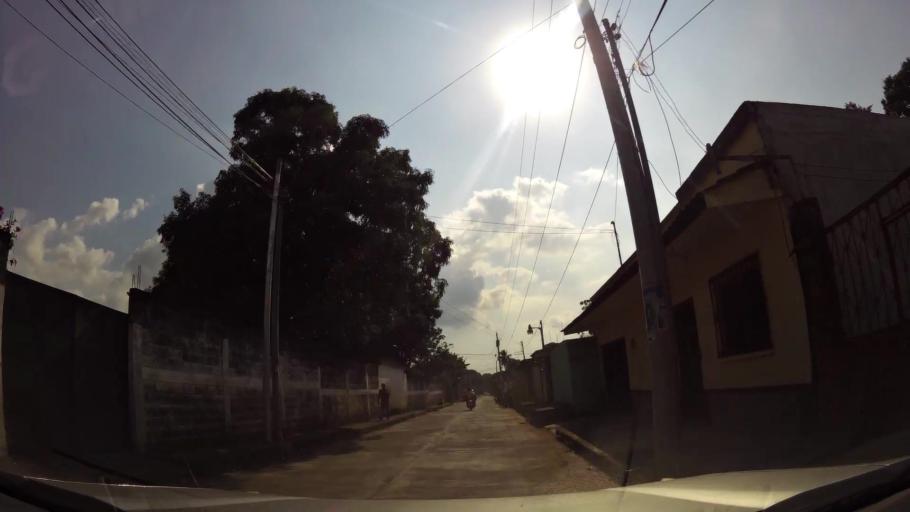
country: GT
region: Retalhuleu
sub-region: Municipio de Retalhuleu
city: Retalhuleu
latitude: 14.5411
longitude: -91.6867
